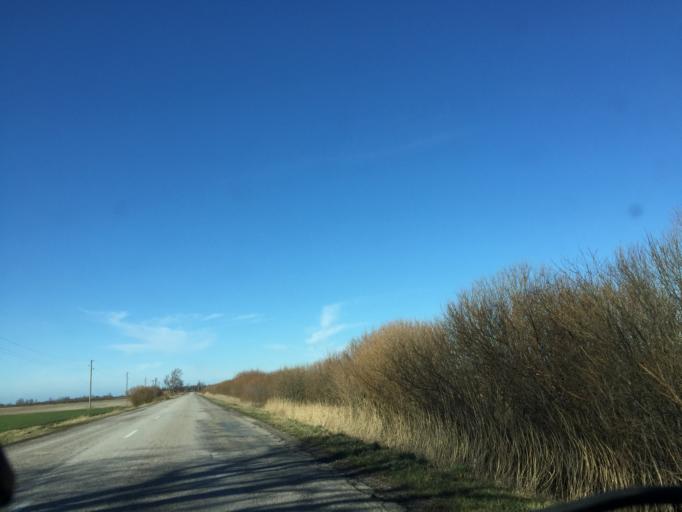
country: LV
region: Ventspils Rajons
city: Piltene
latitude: 57.3012
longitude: 21.6442
